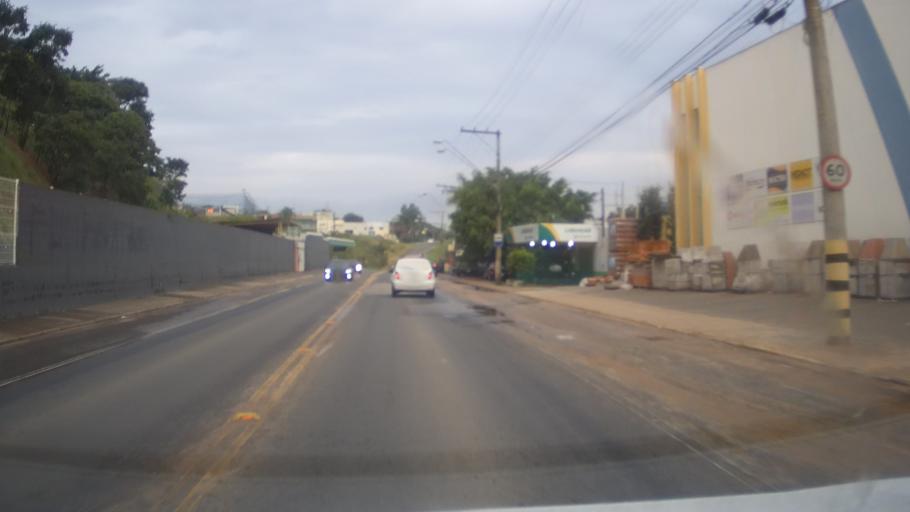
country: BR
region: Sao Paulo
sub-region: Valinhos
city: Valinhos
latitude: -22.9488
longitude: -46.9841
